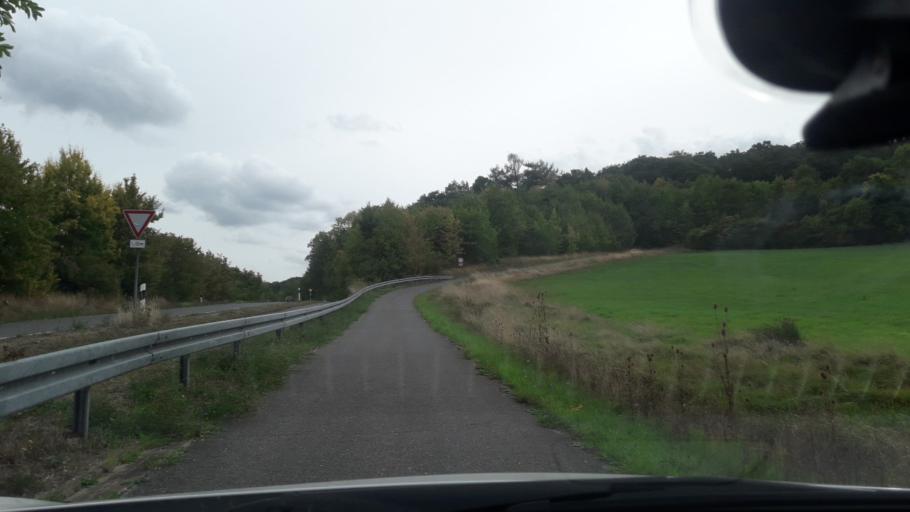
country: DE
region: Lower Saxony
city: Elbe
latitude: 52.0902
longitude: 10.3655
